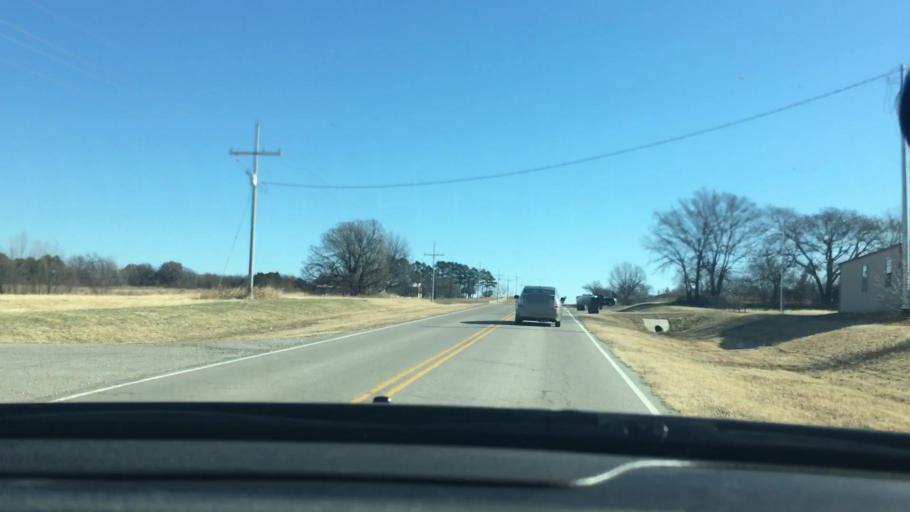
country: US
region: Oklahoma
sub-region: Murray County
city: Davis
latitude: 34.4771
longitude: -97.0589
